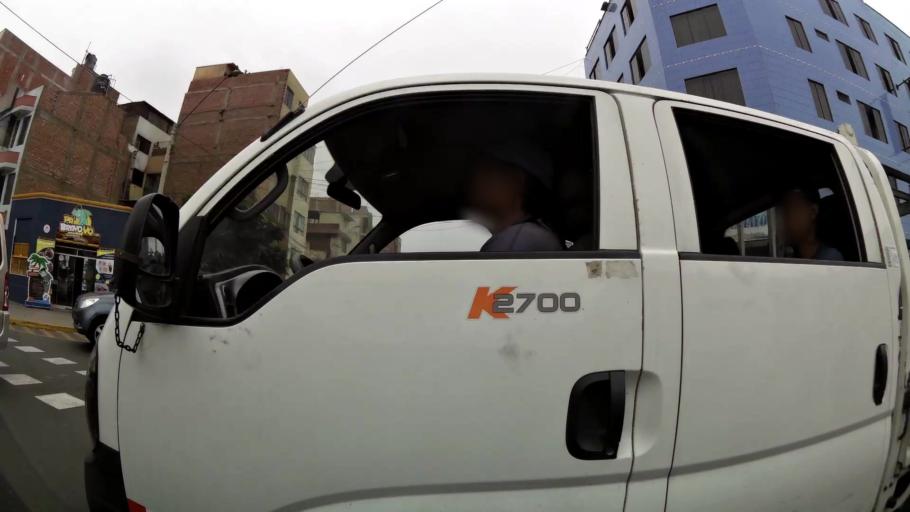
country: PE
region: Lima
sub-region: Lima
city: San Isidro
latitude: -12.0853
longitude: -77.0312
